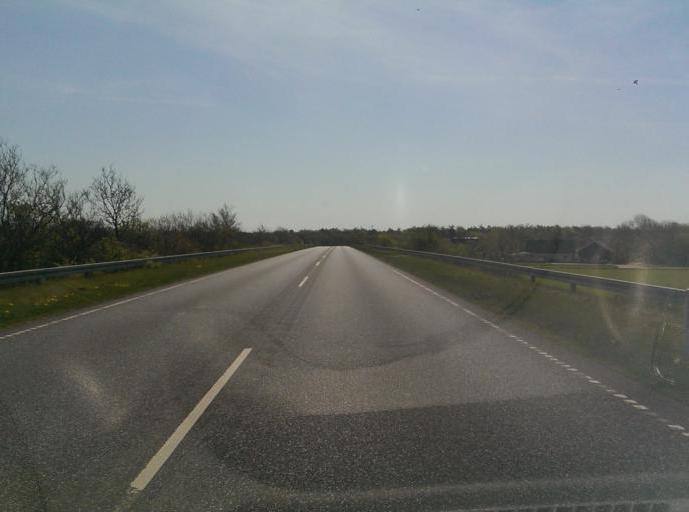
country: DK
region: South Denmark
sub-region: Esbjerg Kommune
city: Ribe
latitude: 55.3970
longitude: 8.7314
